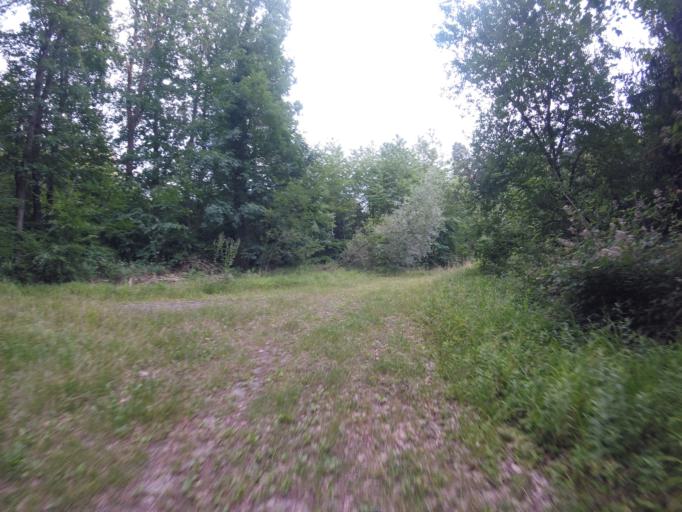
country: DE
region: Baden-Wuerttemberg
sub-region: Regierungsbezirk Stuttgart
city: Sulzbach an der Murr
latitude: 48.9717
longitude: 9.4955
